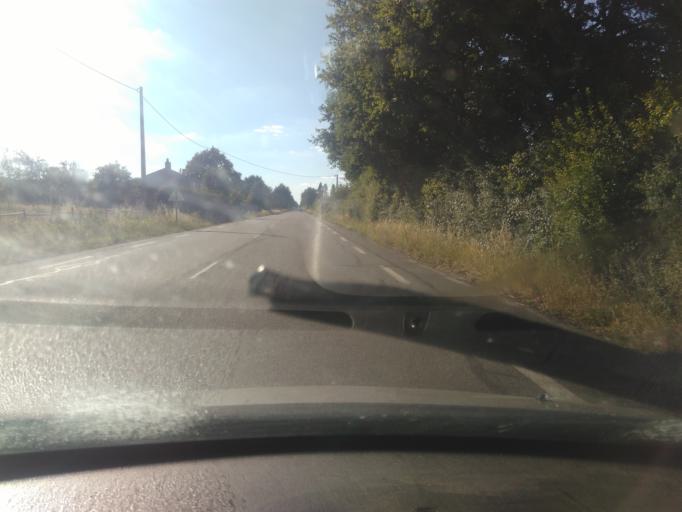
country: FR
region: Pays de la Loire
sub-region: Departement de la Vendee
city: Saint-Florent-des-Bois
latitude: 46.6064
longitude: -1.3386
